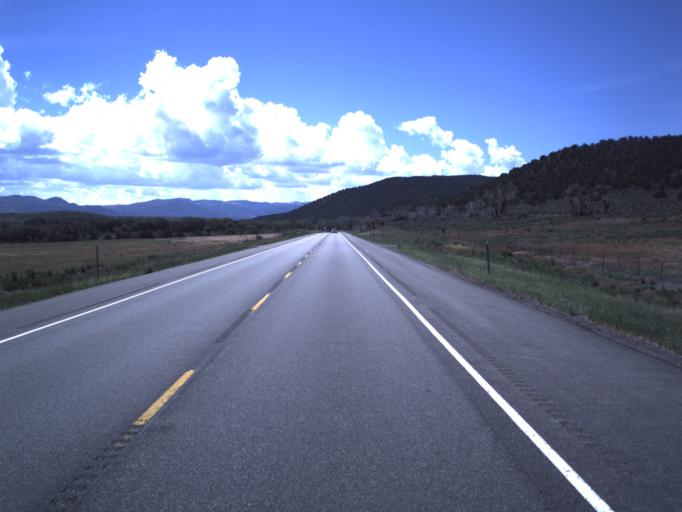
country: US
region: Utah
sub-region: Garfield County
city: Panguitch
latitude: 37.8134
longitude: -112.4032
